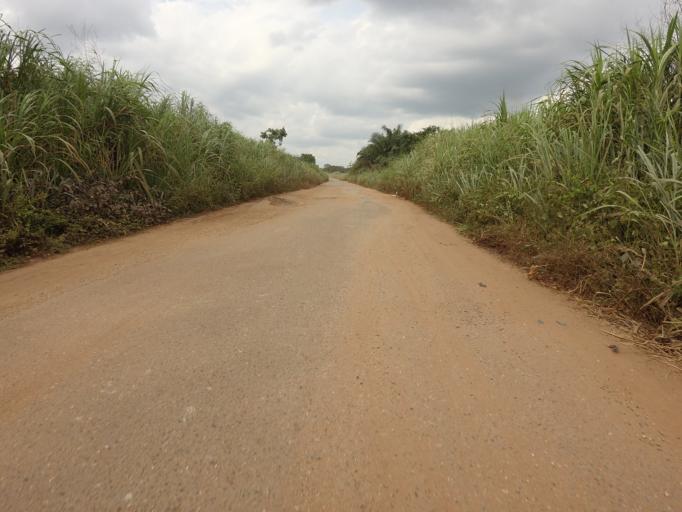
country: GH
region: Volta
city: Ho
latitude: 6.6572
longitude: 0.3459
